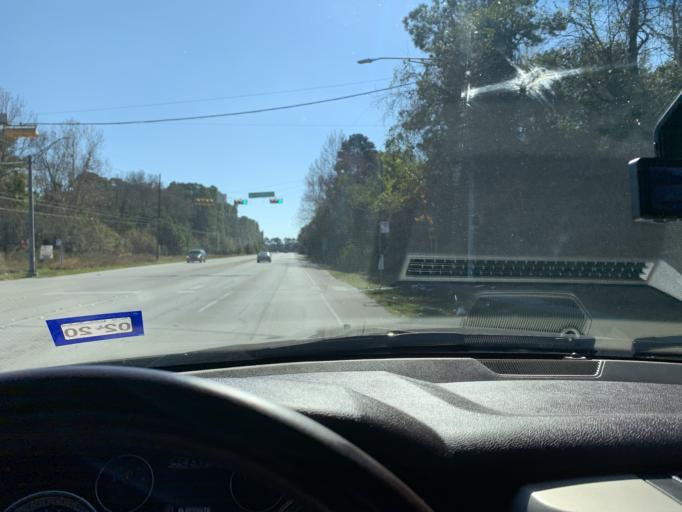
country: US
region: Texas
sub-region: Harris County
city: Spring
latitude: 30.0017
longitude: -95.4408
